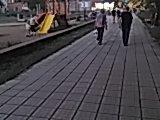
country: RU
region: Orenburg
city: Novotroitsk
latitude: 51.1928
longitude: 58.2931
